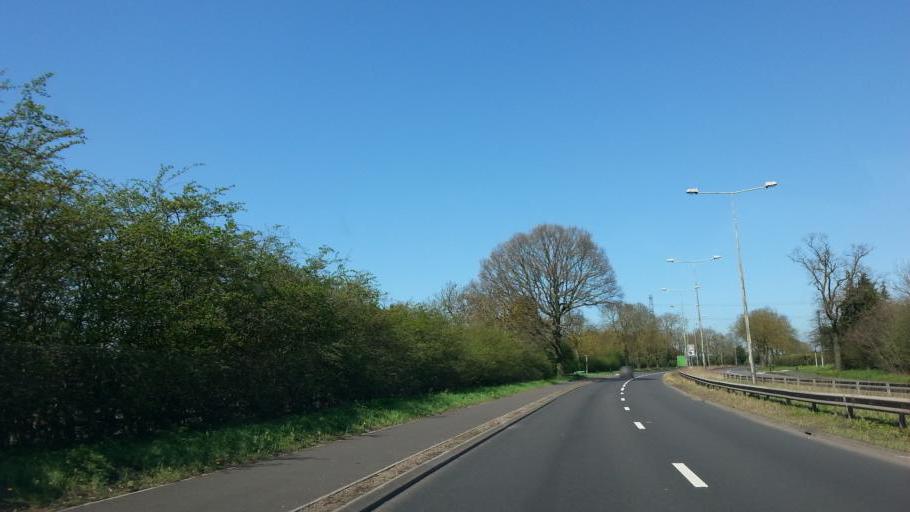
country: GB
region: England
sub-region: Staffordshire
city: Featherstone
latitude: 52.6610
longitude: -2.1313
